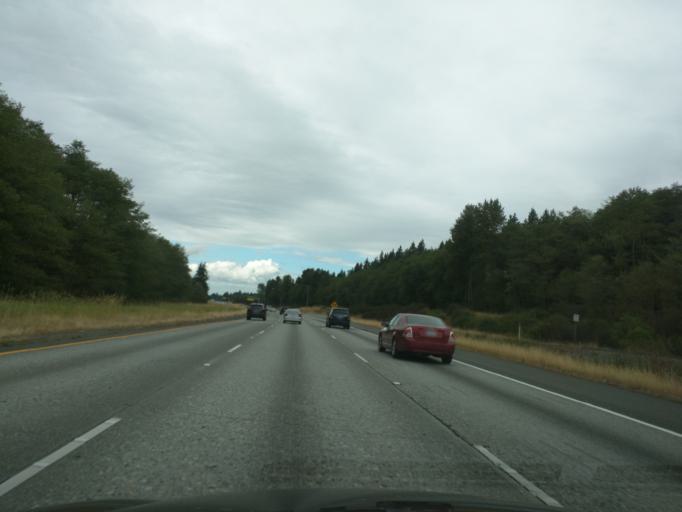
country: US
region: Washington
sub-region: Snohomish County
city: Bryant
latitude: 48.2596
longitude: -122.2593
